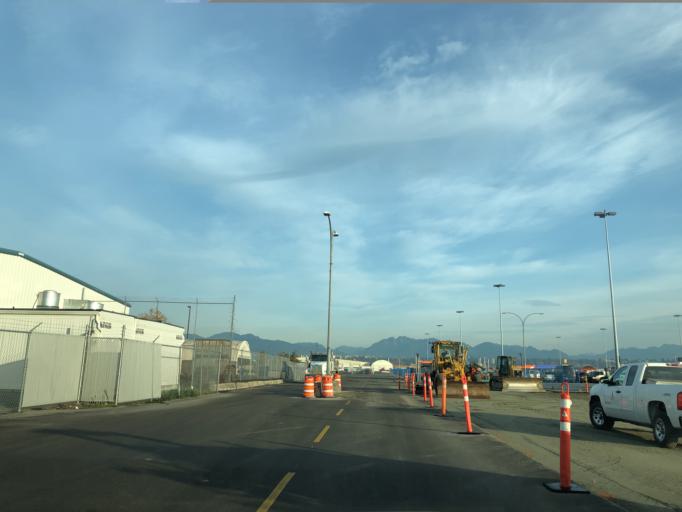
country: CA
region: British Columbia
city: Richmond
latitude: 49.1941
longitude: -123.1675
